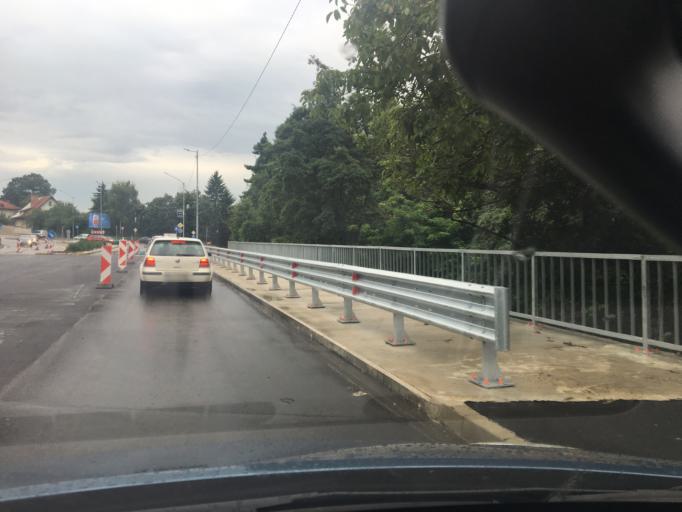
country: BG
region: Sofia-Capital
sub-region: Stolichna Obshtina
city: Sofia
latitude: 42.6492
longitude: 23.2670
